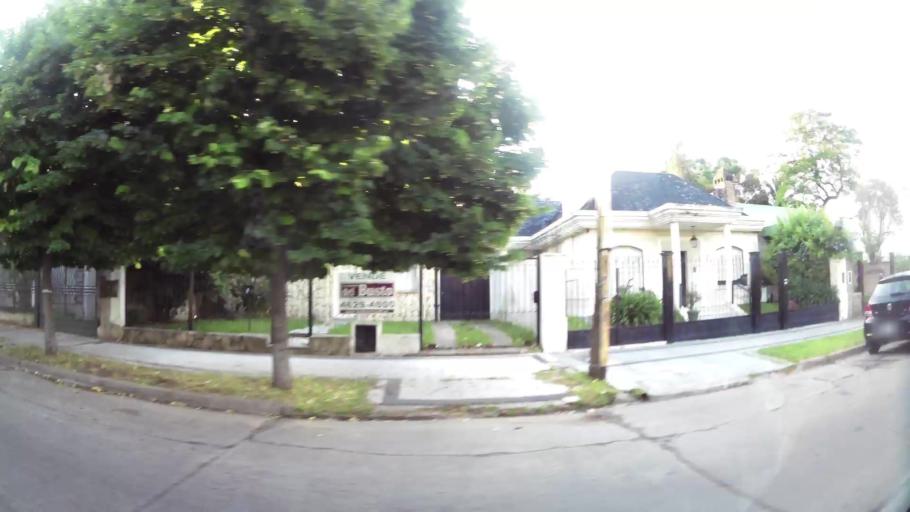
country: AR
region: Buenos Aires
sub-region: Partido de Moron
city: Moron
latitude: -34.6525
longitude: -58.6140
